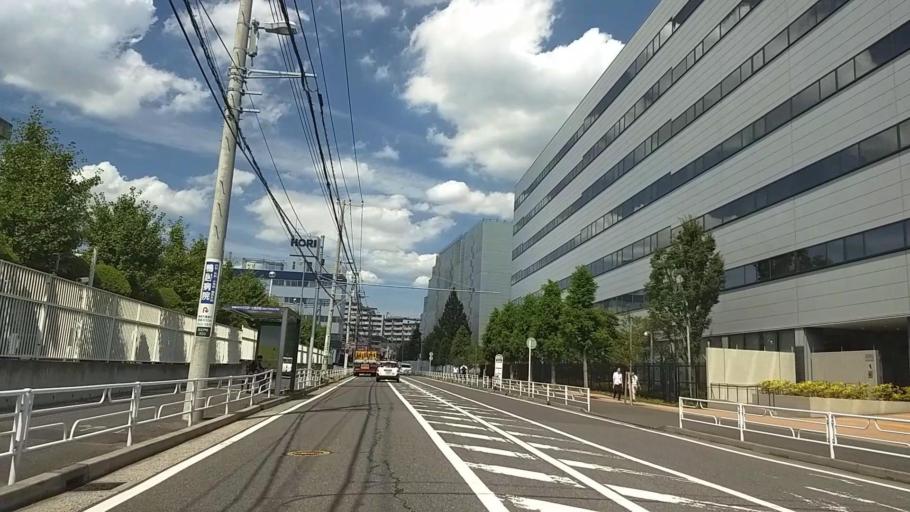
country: JP
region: Kanagawa
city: Yokohama
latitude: 35.5161
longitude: 139.5636
